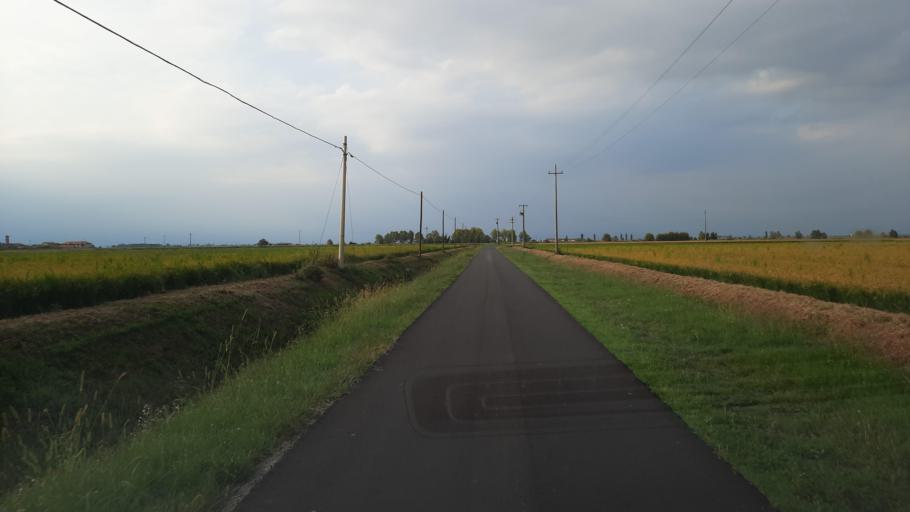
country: IT
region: Piedmont
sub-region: Provincia di Vercelli
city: Sali Vercellese
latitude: 45.3183
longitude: 8.3482
